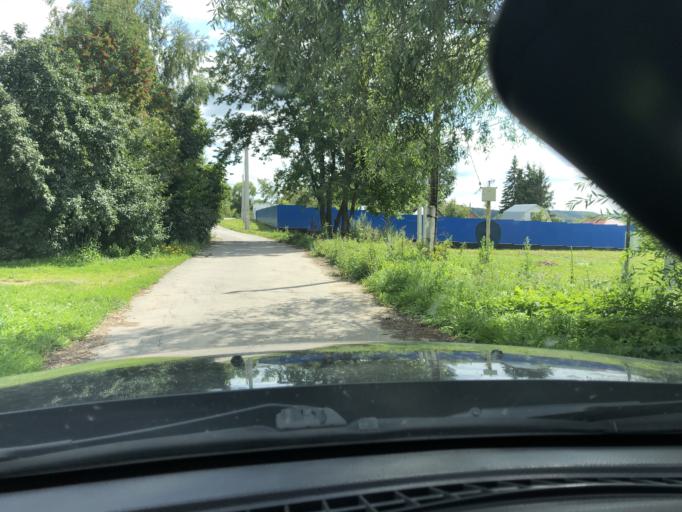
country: RU
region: Tula
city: Revyakino
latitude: 54.3484
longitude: 37.6163
